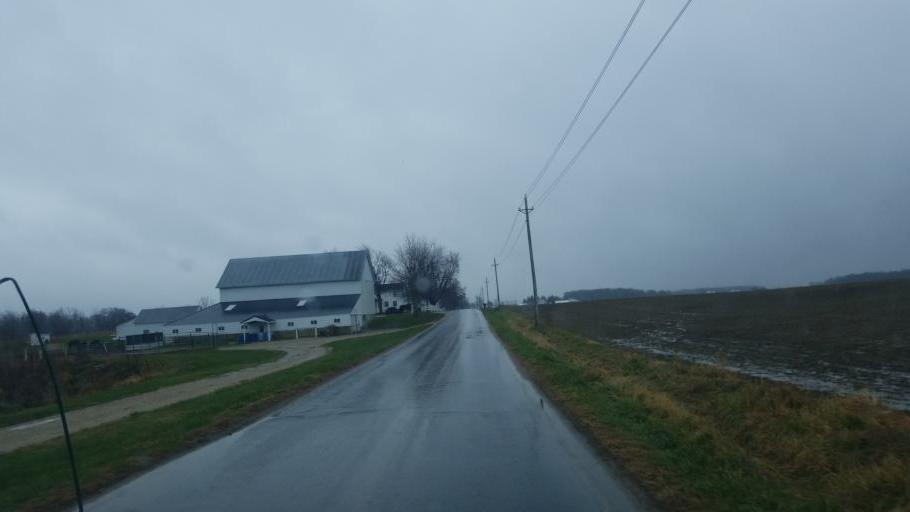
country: US
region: Indiana
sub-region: Adams County
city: Berne
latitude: 40.6506
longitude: -84.8785
